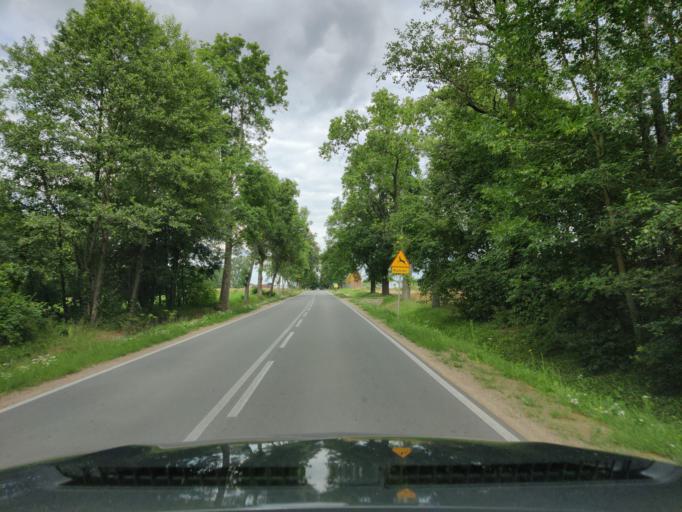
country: PL
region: Masovian Voivodeship
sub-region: Powiat sokolowski
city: Ceranow
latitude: 52.6218
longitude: 22.2124
